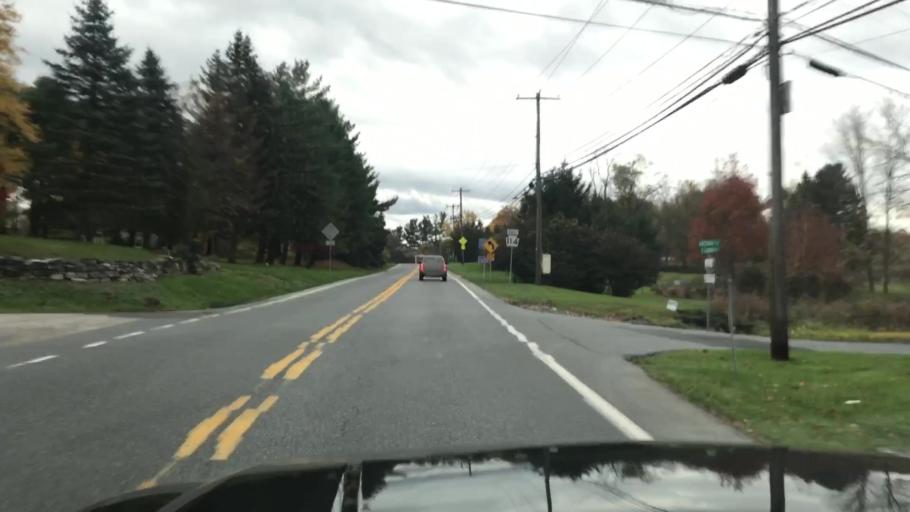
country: US
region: Pennsylvania
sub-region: Cumberland County
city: Shiremanstown
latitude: 40.1733
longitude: -76.9438
